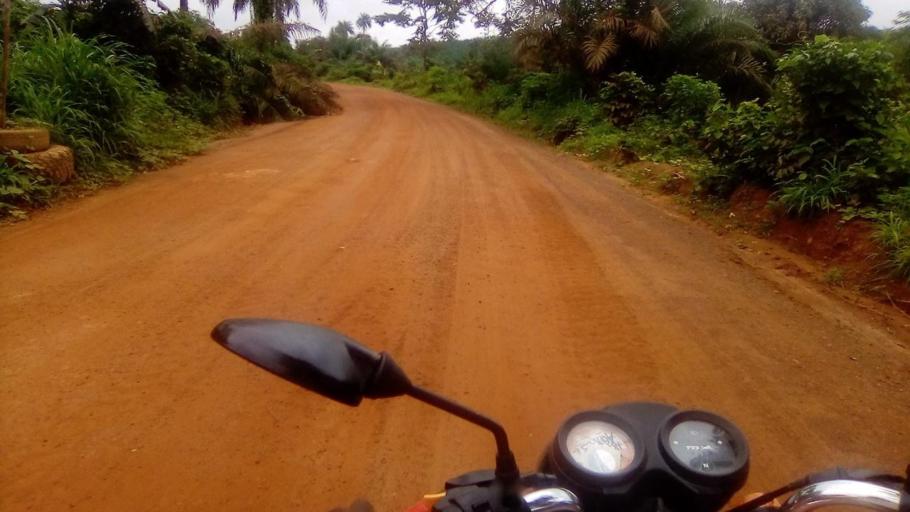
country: SL
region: Southern Province
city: Tongole
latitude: 7.4388
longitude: -11.8637
